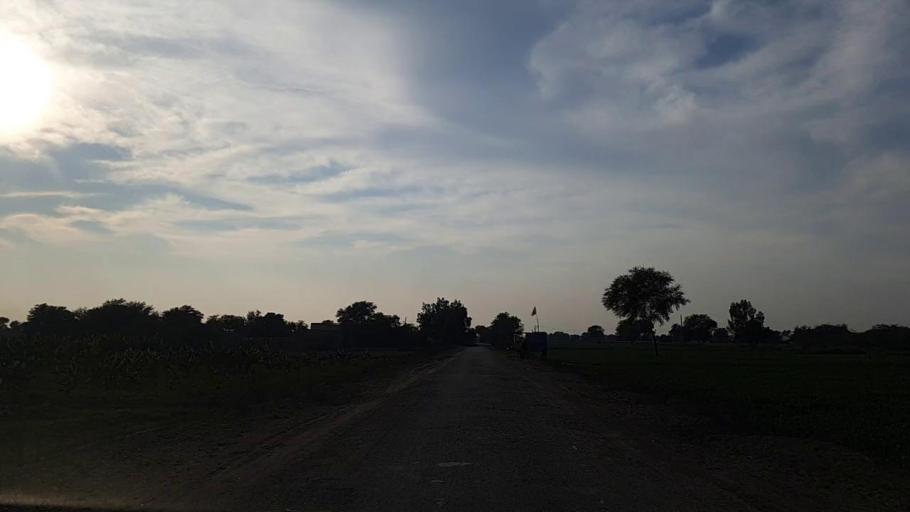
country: PK
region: Sindh
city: Bandhi
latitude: 26.5645
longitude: 68.2731
